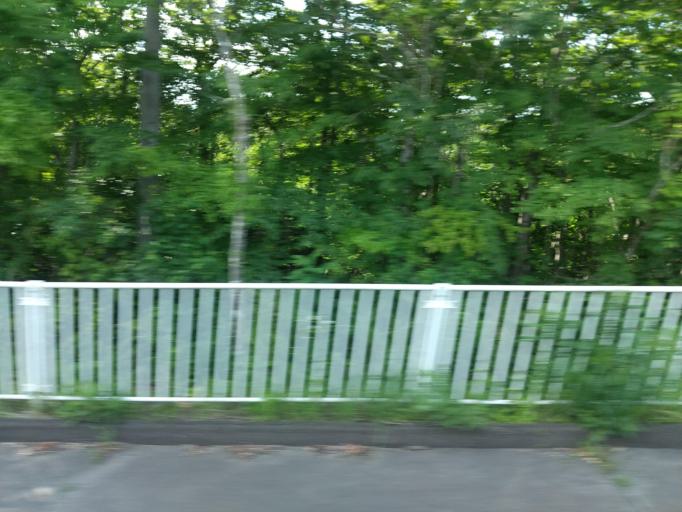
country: JP
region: Miyagi
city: Sendai
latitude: 38.2407
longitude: 140.7331
